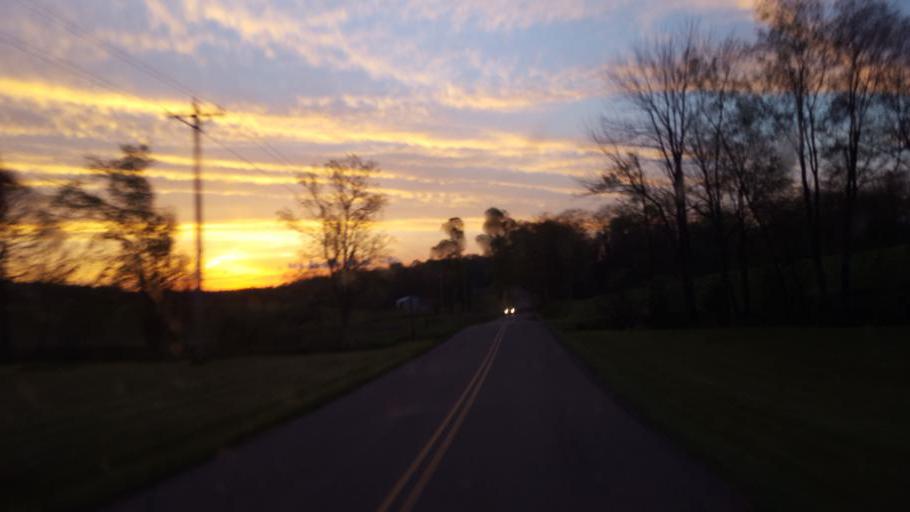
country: US
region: Ohio
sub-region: Knox County
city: Mount Vernon
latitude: 40.4721
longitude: -82.4253
